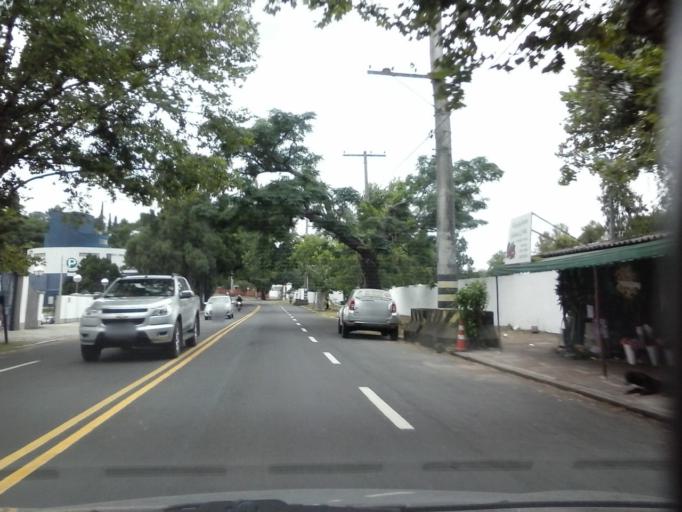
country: BR
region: Rio Grande do Sul
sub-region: Porto Alegre
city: Porto Alegre
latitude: -30.0560
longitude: -51.2106
